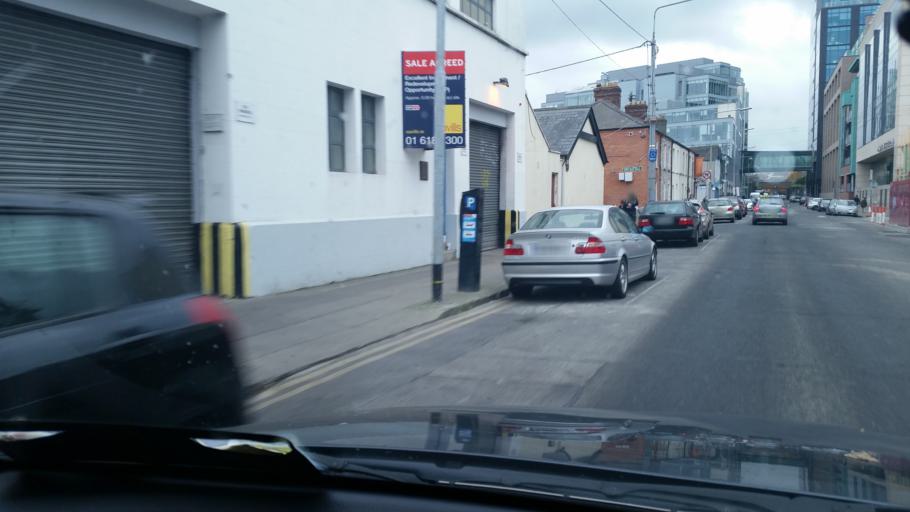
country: IE
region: Leinster
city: Ringsend
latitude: 53.3415
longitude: -6.2362
